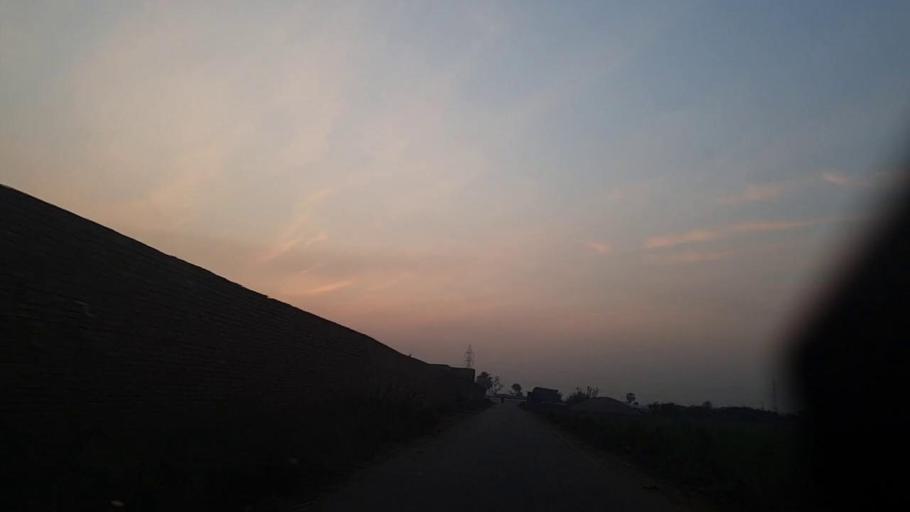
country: PK
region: Sindh
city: Sakrand
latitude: 26.1019
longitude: 68.3001
